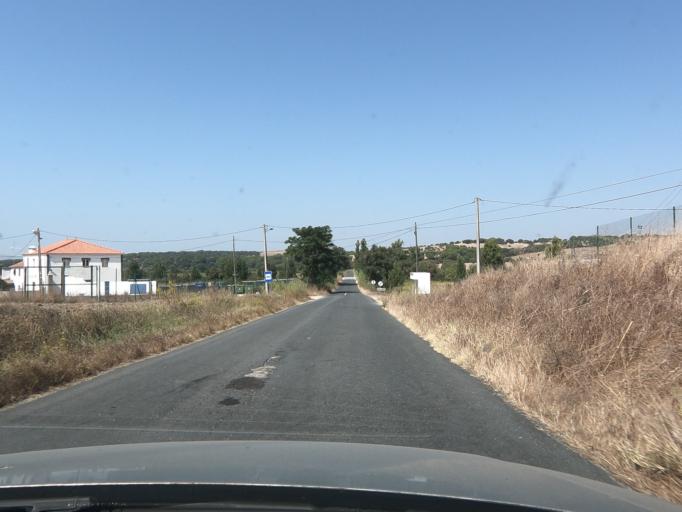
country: PT
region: Setubal
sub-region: Alcacer do Sal
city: Alcacer do Sal
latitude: 38.2834
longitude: -8.4000
